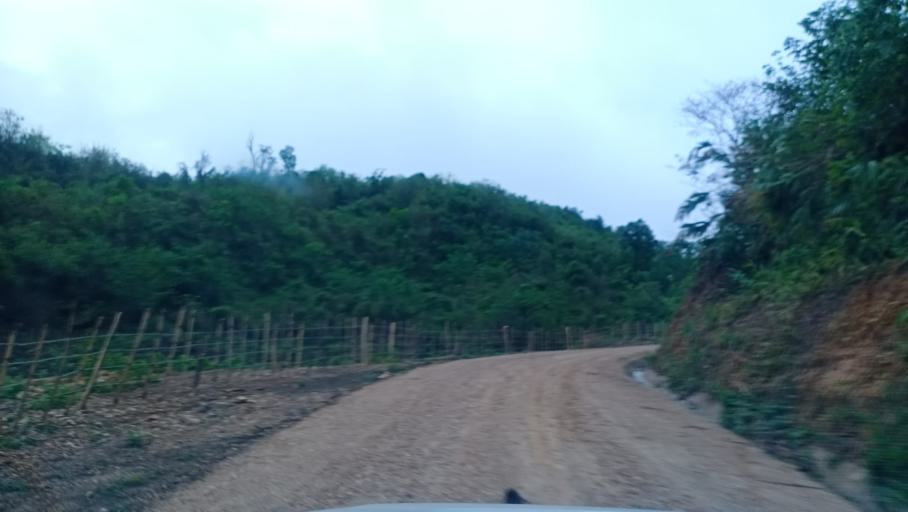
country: LA
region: Phongsali
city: Khoa
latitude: 21.2310
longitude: 102.6903
